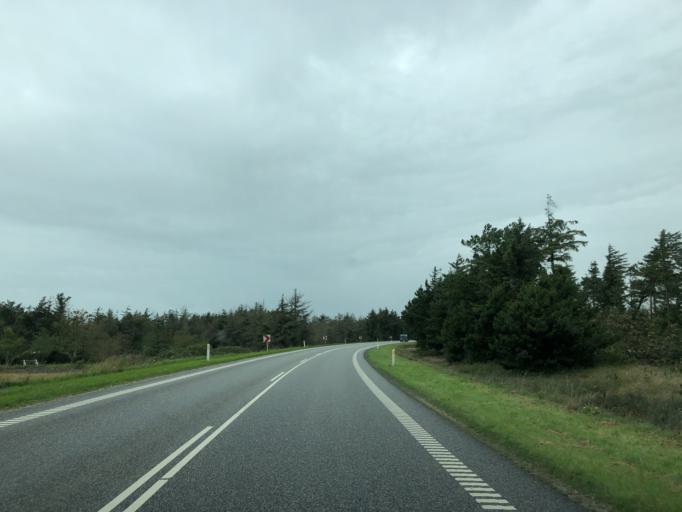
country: DK
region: Central Jutland
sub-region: Struer Kommune
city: Struer
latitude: 56.5847
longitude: 8.5314
